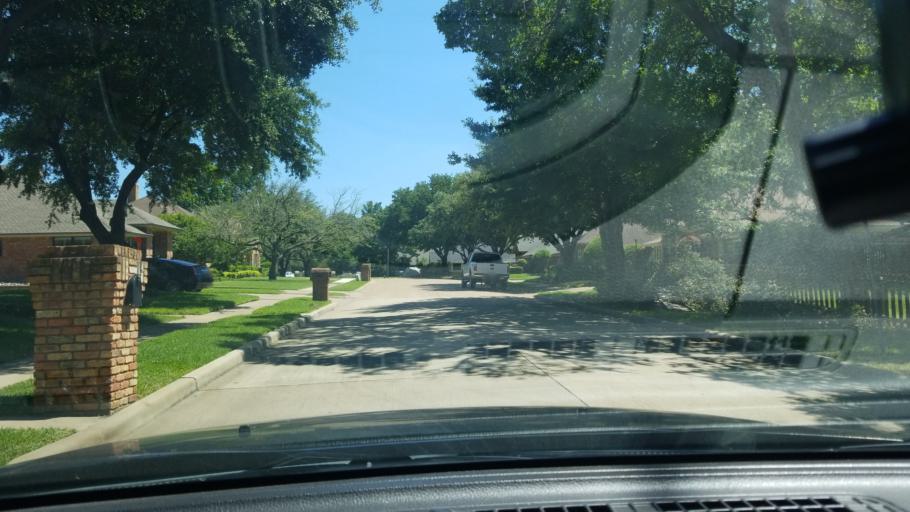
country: US
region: Texas
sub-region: Dallas County
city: Mesquite
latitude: 32.7578
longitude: -96.6042
